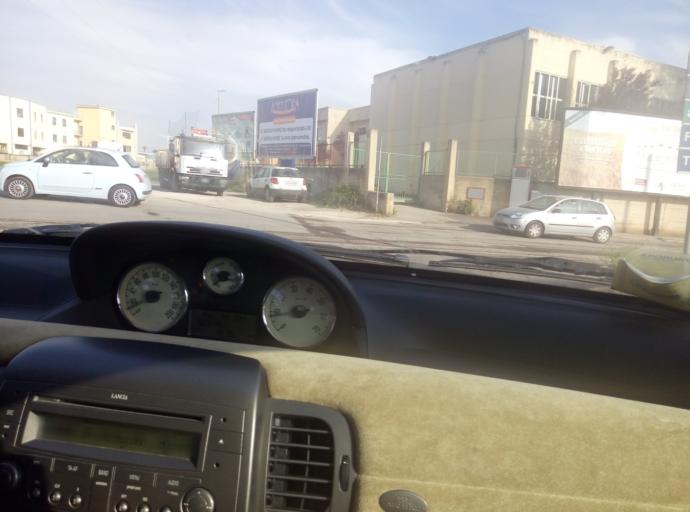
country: IT
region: Apulia
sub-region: Provincia di Bari
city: Corato
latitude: 41.1452
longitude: 16.4048
